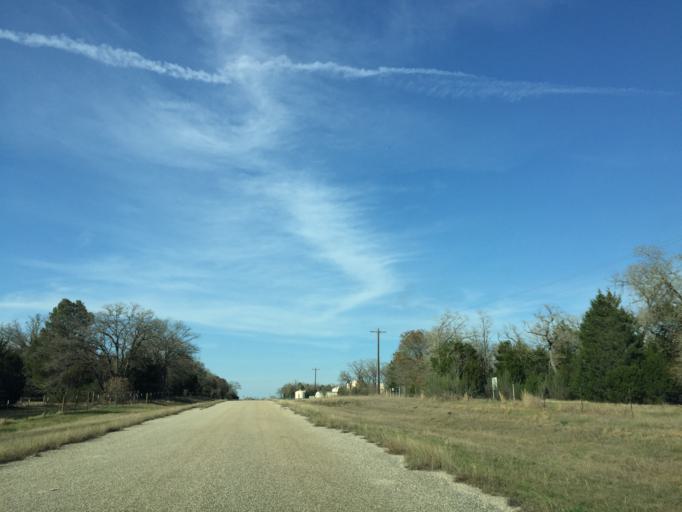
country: US
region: Texas
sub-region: Lee County
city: Lexington
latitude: 30.4476
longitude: -97.1697
